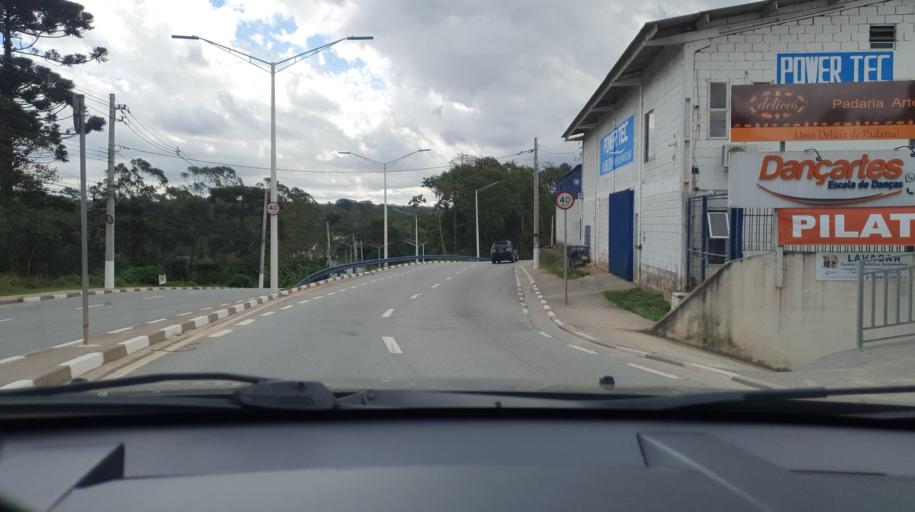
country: BR
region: Sao Paulo
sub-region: Vargem Grande Paulista
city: Vargem Grande Paulista
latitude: -23.6264
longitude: -46.9827
